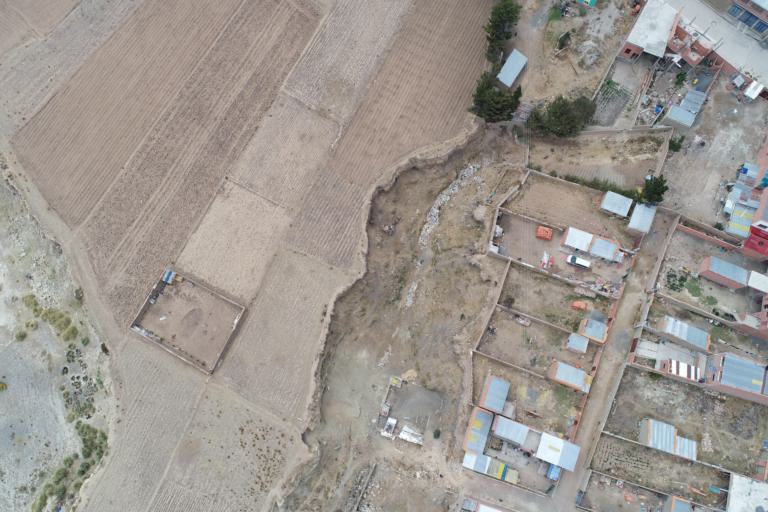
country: BO
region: La Paz
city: Achacachi
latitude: -16.0400
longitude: -68.6830
